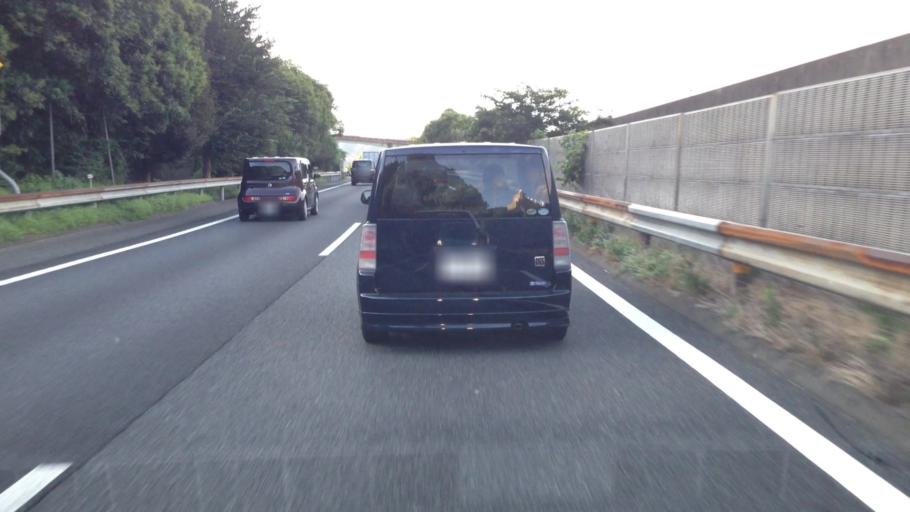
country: JP
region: Kanagawa
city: Zushi
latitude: 35.3154
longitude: 139.6067
